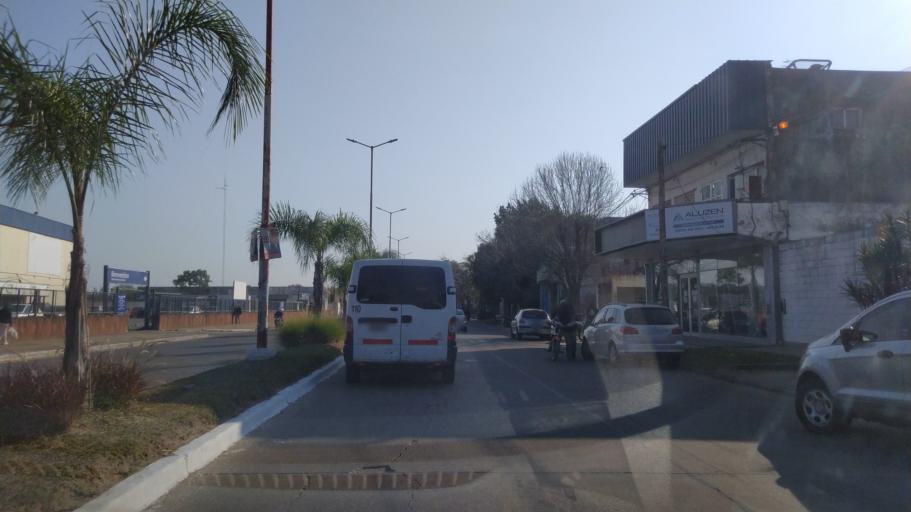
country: AR
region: Corrientes
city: Corrientes
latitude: -27.4777
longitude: -58.8144
